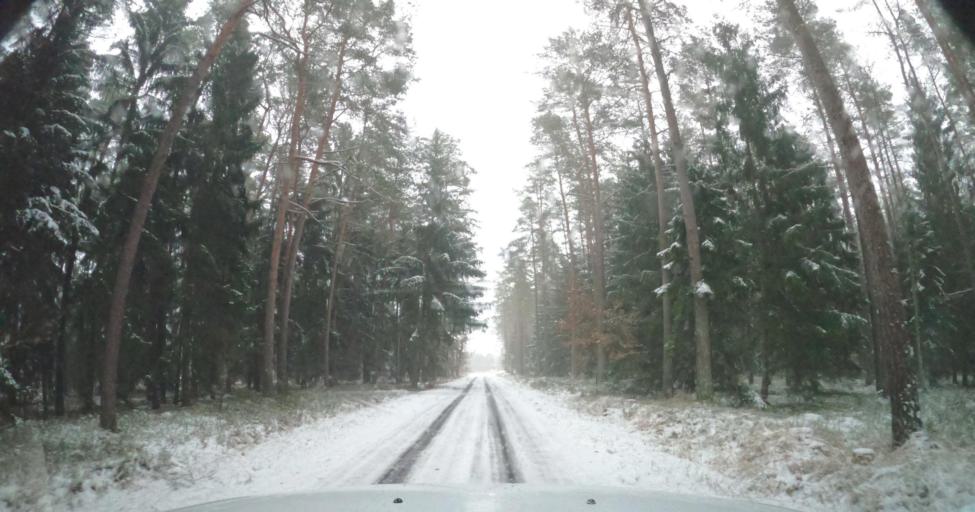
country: PL
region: West Pomeranian Voivodeship
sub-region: Powiat goleniowski
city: Przybiernow
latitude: 53.6611
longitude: 14.7888
